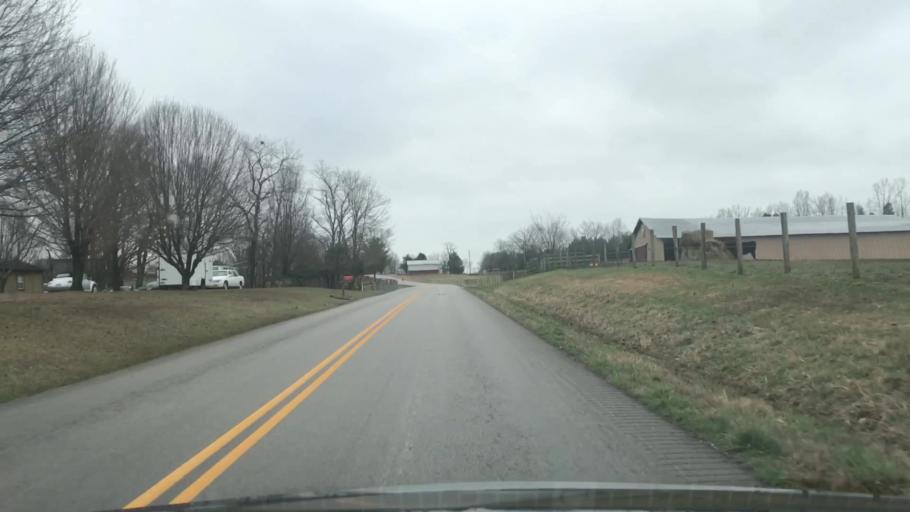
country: US
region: Kentucky
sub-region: Barren County
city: Glasgow
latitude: 36.9093
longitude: -85.7986
